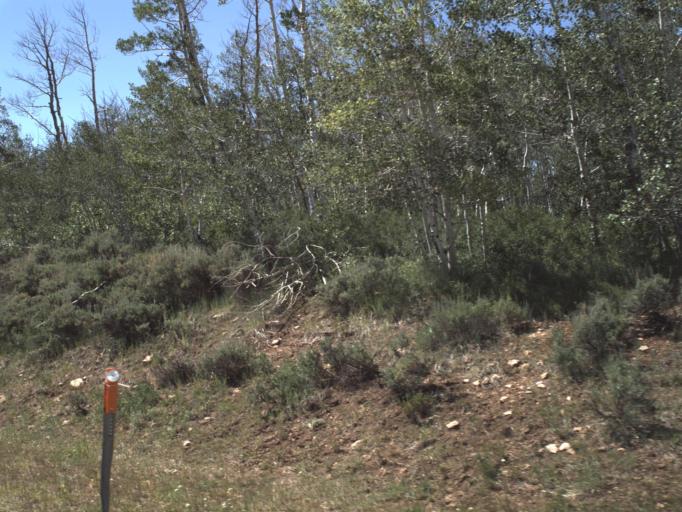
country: US
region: Utah
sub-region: Rich County
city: Randolph
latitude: 41.4741
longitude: -111.4430
